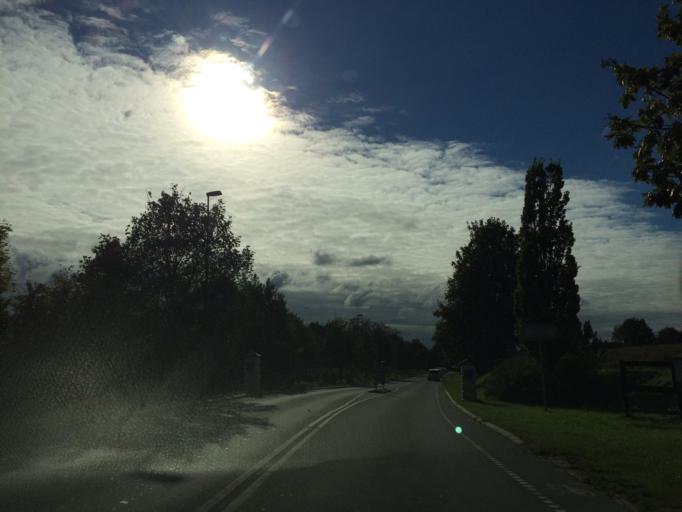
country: DK
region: Central Jutland
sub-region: Skanderborg Kommune
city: Ry
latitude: 56.0789
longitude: 9.7054
